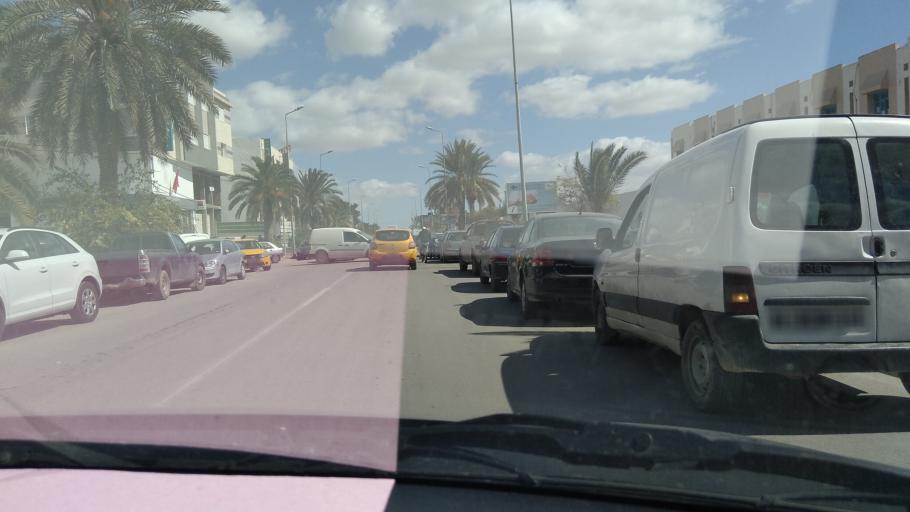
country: TN
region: Al Qayrawan
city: Kairouan
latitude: 35.6844
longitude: 10.0938
